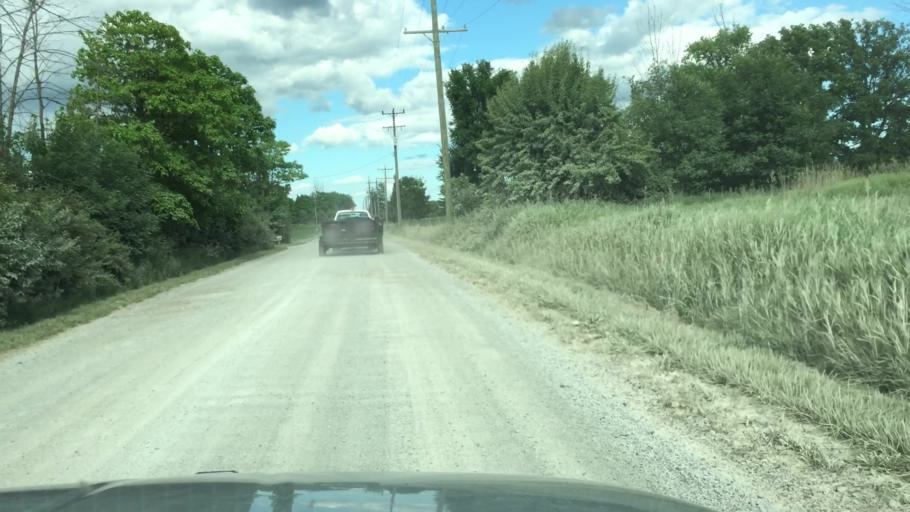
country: US
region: Michigan
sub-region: Saint Clair County
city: Yale
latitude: 43.1440
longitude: -82.8154
